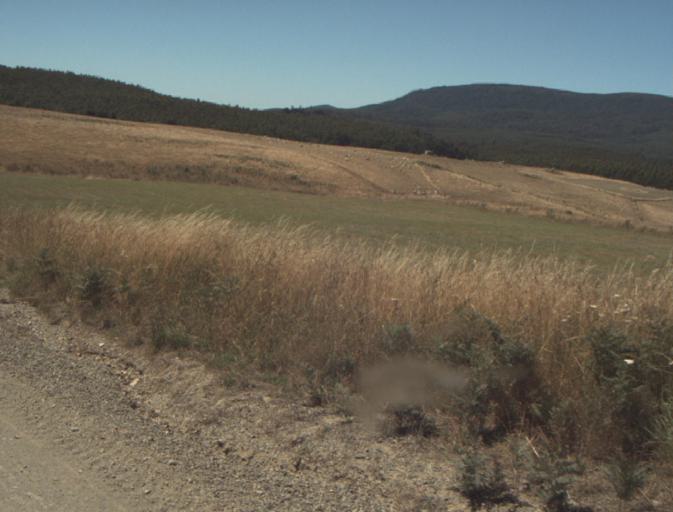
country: AU
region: Tasmania
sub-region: Dorset
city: Scottsdale
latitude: -41.3271
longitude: 147.4442
